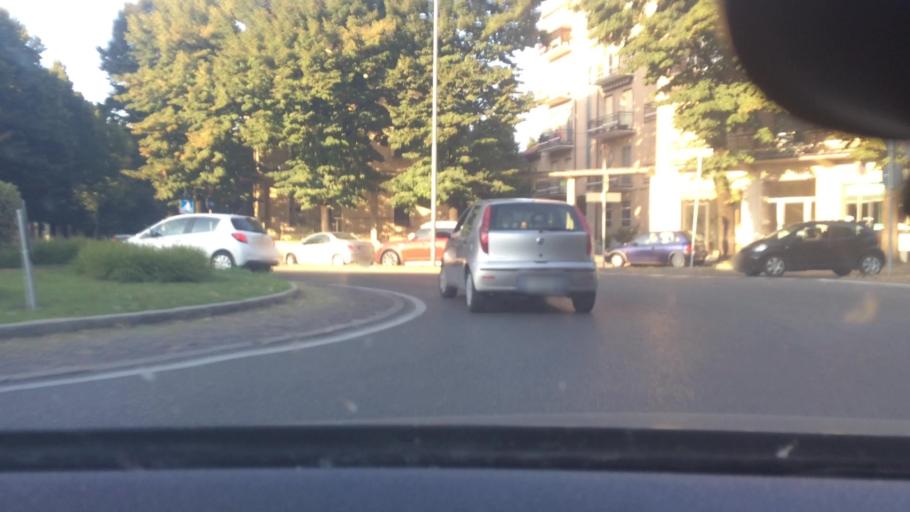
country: IT
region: Emilia-Romagna
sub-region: Provincia di Piacenza
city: Piacenza
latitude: 45.0455
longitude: 9.7040
